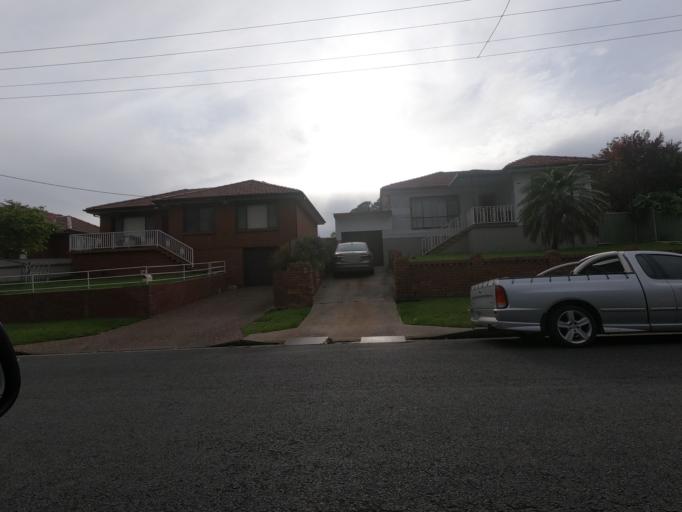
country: AU
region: New South Wales
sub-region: Wollongong
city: Lake Heights
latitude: -34.4833
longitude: 150.8689
